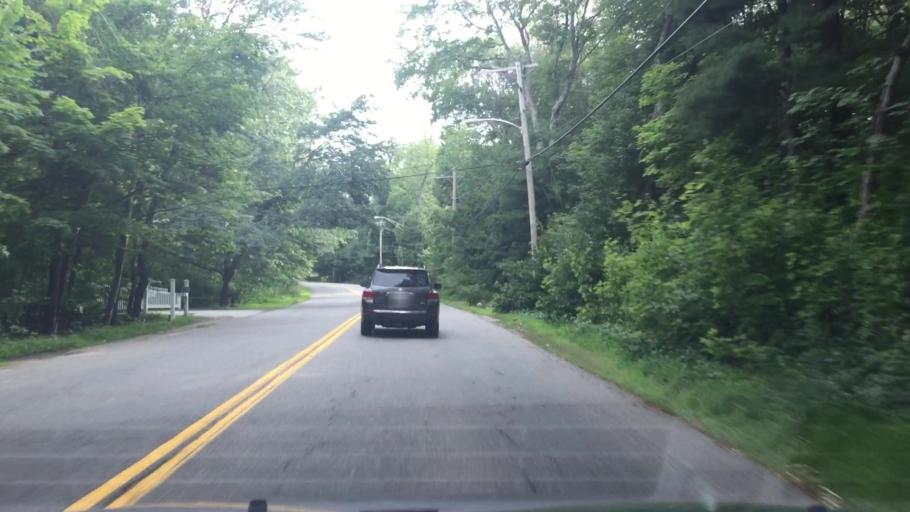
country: US
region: New Hampshire
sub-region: Rockingham County
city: Salem
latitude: 42.7905
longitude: -71.1545
